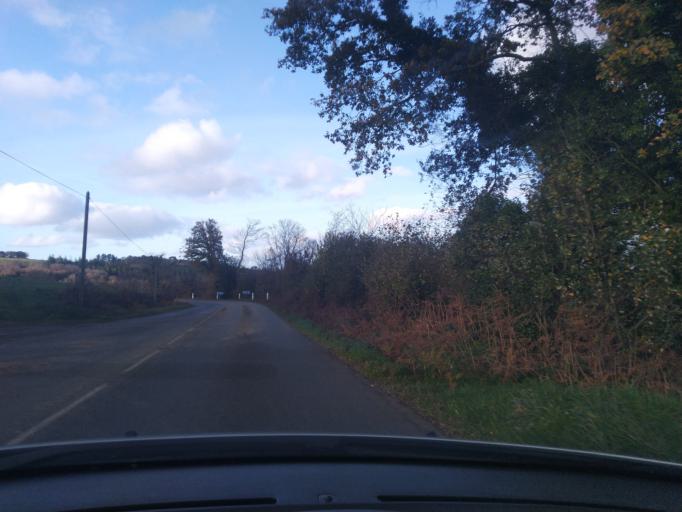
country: FR
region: Brittany
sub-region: Departement du Finistere
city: Plouigneau
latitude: 48.5736
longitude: -3.6523
